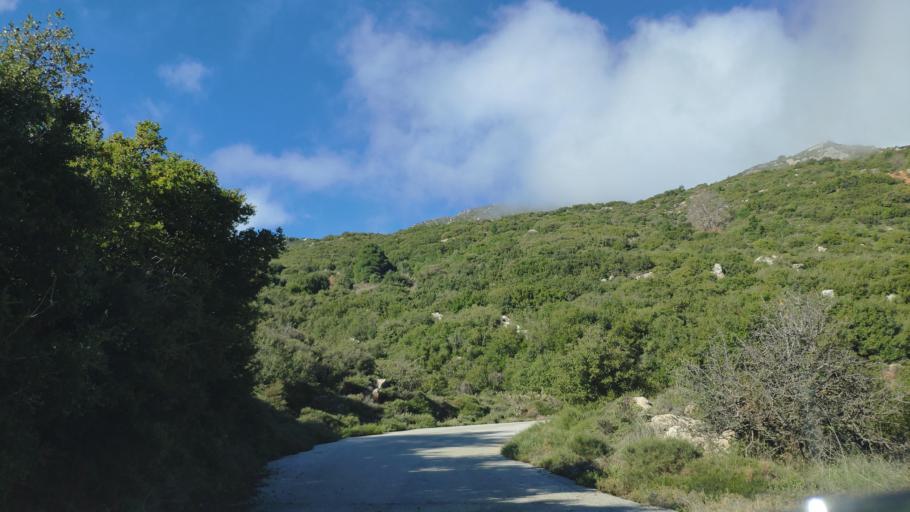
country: GR
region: West Greece
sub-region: Nomos Achaias
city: Aiyira
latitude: 38.0570
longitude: 22.4544
